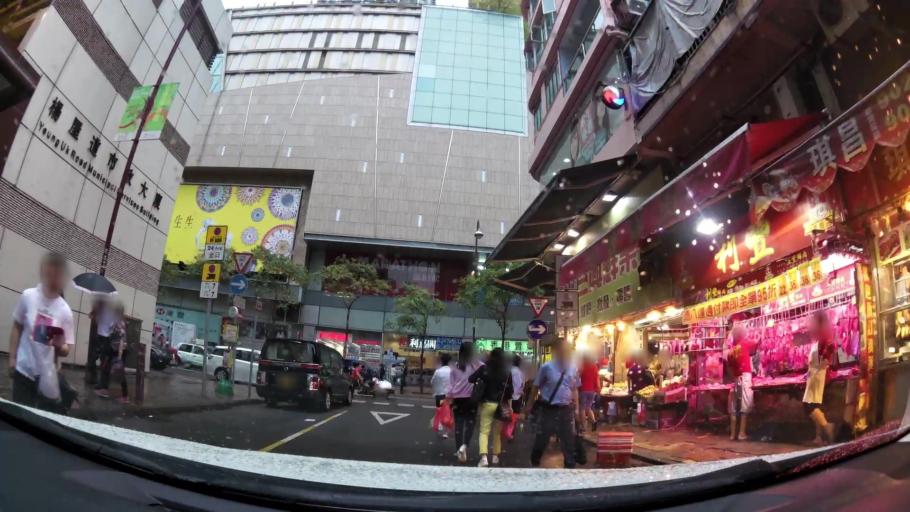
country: HK
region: Tsuen Wan
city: Tsuen Wan
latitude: 22.3692
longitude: 114.1147
